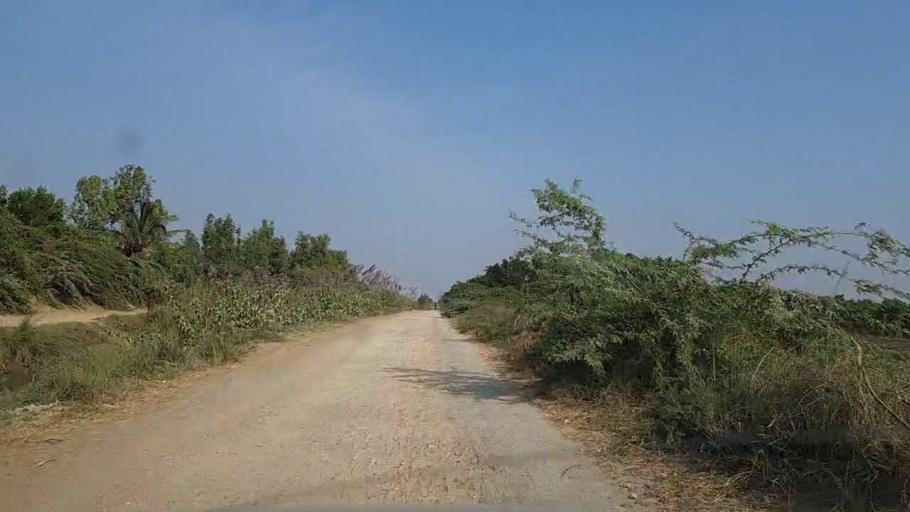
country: PK
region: Sindh
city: Mirpur Sakro
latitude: 24.5936
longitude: 67.5780
